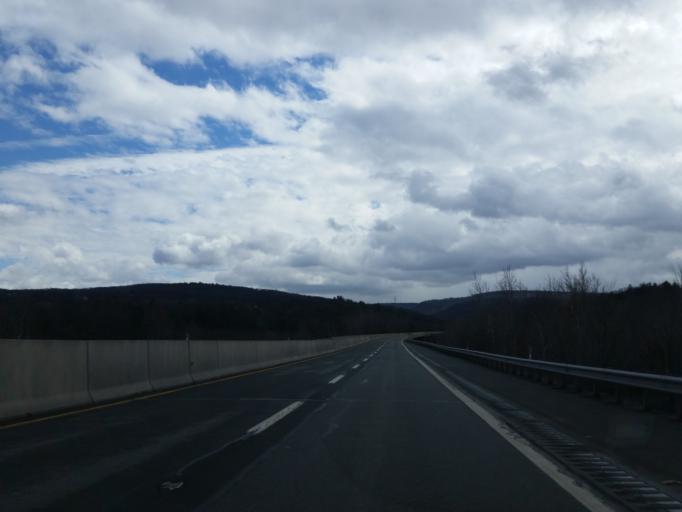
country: US
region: Pennsylvania
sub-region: Lackawanna County
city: Moosic
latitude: 41.3511
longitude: -75.7117
